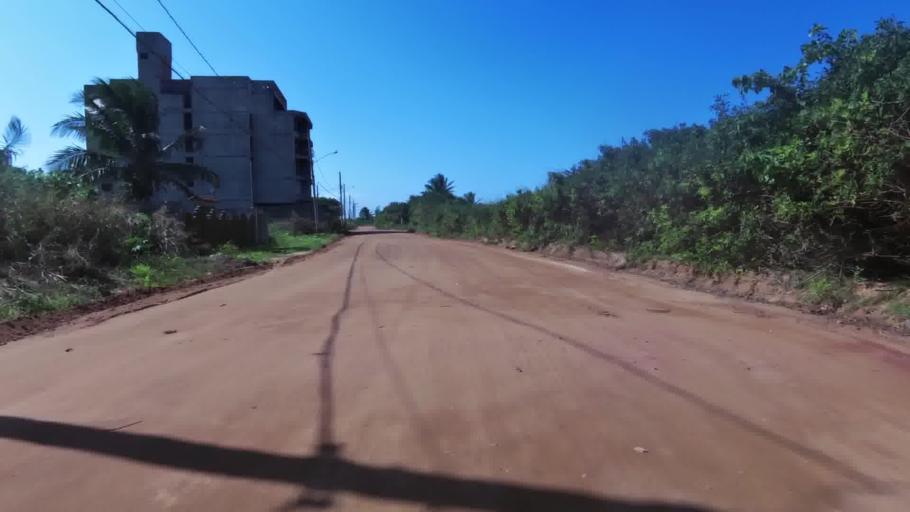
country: BR
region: Espirito Santo
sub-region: Piuma
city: Piuma
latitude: -20.8334
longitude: -40.6216
